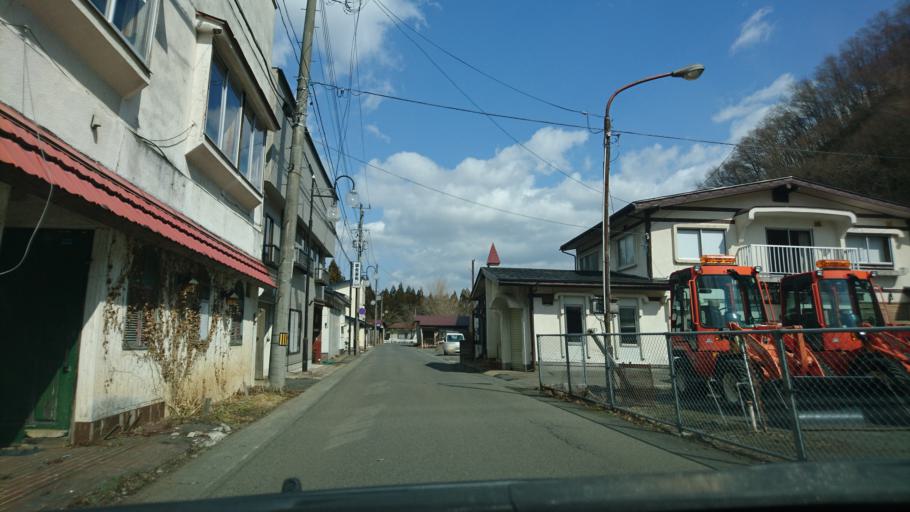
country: JP
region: Iwate
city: Shizukuishi
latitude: 39.6375
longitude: 140.9238
